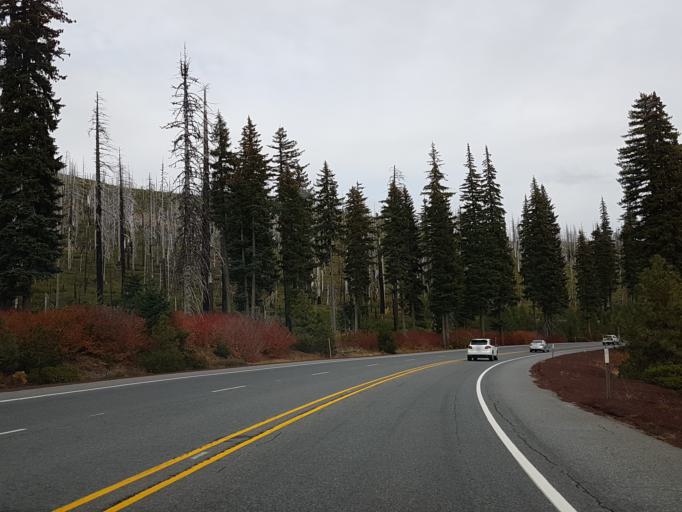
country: US
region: Oregon
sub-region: Deschutes County
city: Sisters
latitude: 44.4237
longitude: -121.8020
